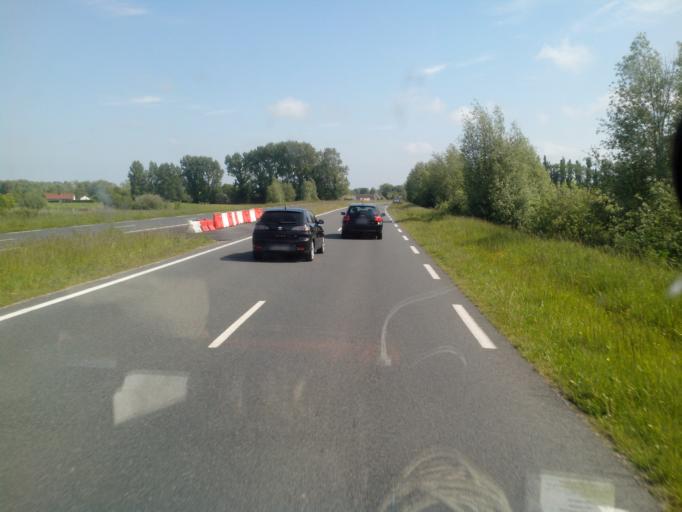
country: FR
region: Picardie
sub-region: Departement de la Somme
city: Rue
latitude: 50.2810
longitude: 1.6581
